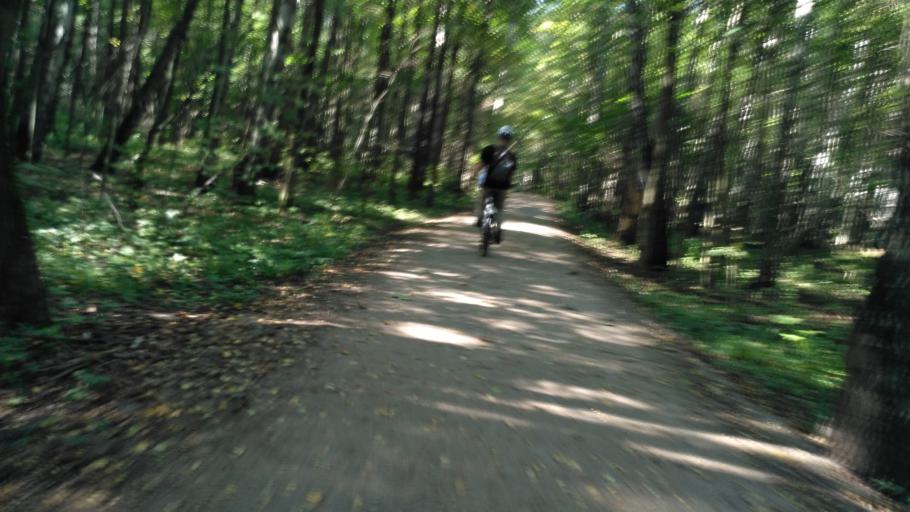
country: RU
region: Moscow
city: Metrogorodok
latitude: 55.7848
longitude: 37.7706
